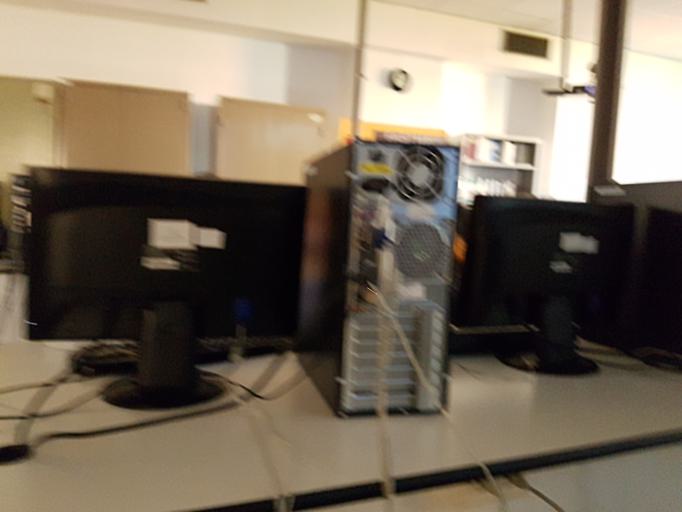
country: IT
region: Lombardy
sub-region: Citta metropolitana di Milano
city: Romano Banco
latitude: 45.4540
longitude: 9.1449
